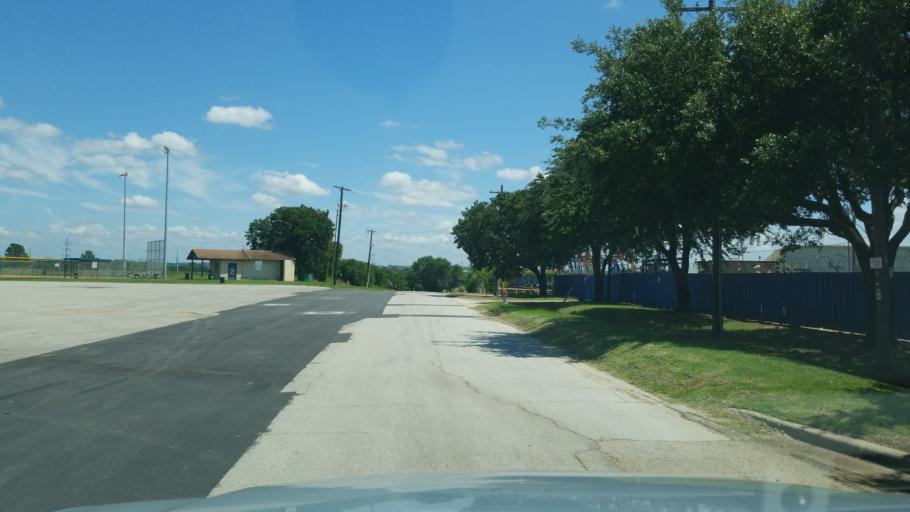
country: US
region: Texas
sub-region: Dallas County
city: Irving
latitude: 32.8001
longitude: -96.9200
